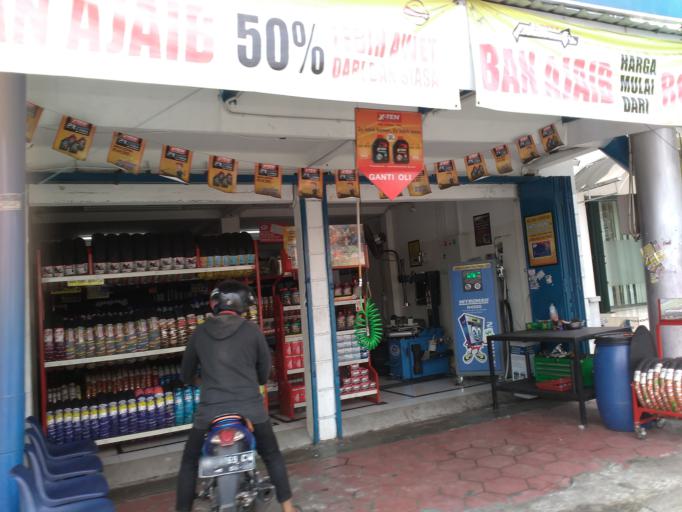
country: ID
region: Central Java
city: Boyolali
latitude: -7.5344
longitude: 110.6011
